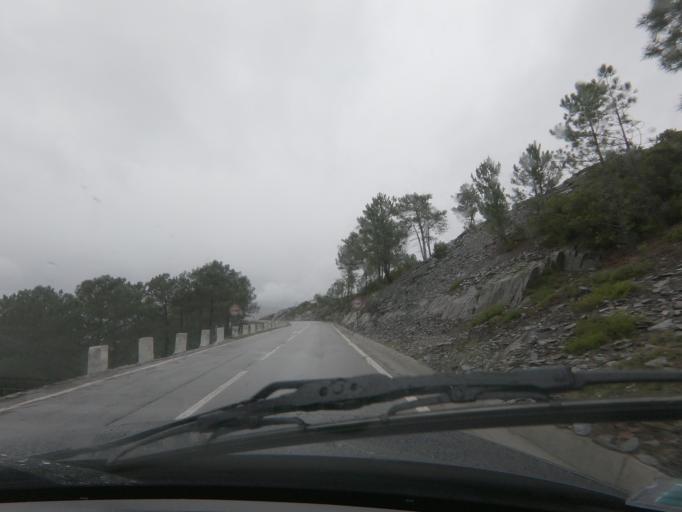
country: PT
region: Vila Real
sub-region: Mondim de Basto
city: Mondim de Basto
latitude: 41.3369
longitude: -7.8769
